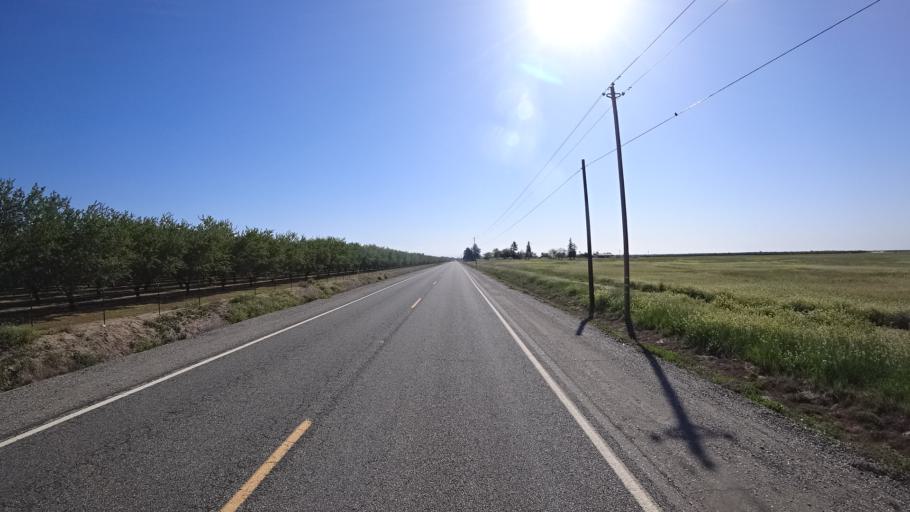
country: US
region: California
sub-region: Glenn County
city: Hamilton City
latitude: 39.7091
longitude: -122.0349
